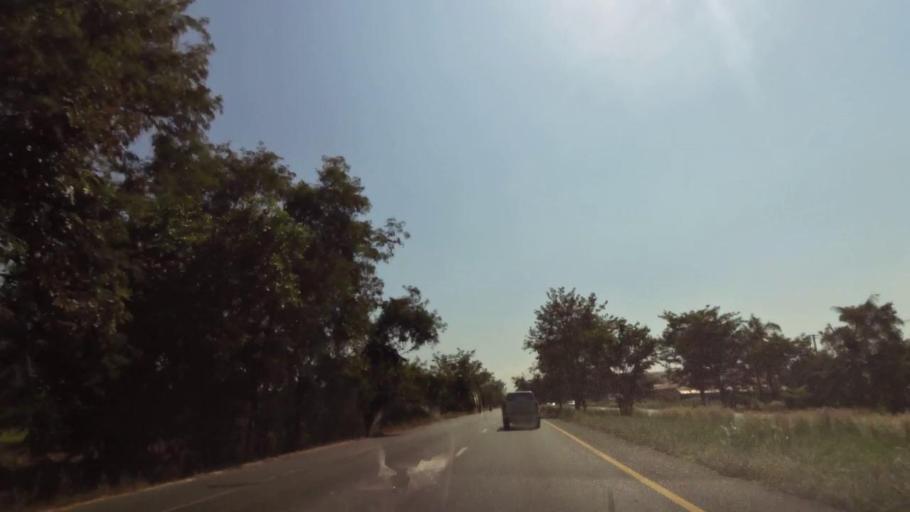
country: TH
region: Nakhon Sawan
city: Kao Liao
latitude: 15.8553
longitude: 100.1170
